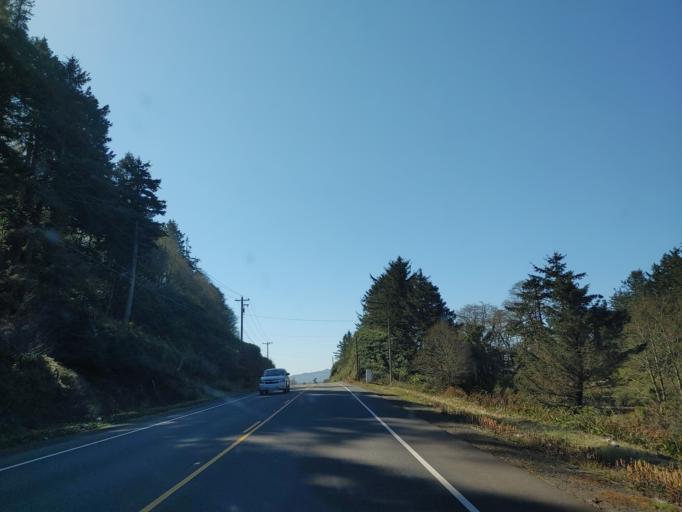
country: US
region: Oregon
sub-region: Tillamook County
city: Rockaway Beach
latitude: 45.5741
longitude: -123.9444
